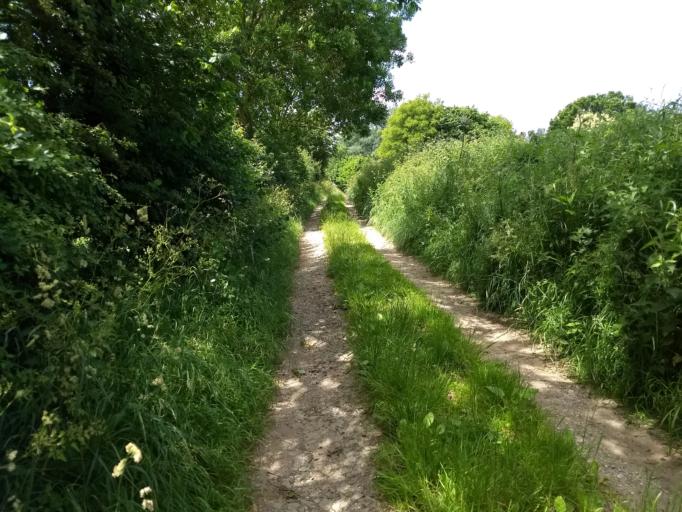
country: GB
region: England
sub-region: Milton Keynes
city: Calverton
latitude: 52.0223
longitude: -0.8679
